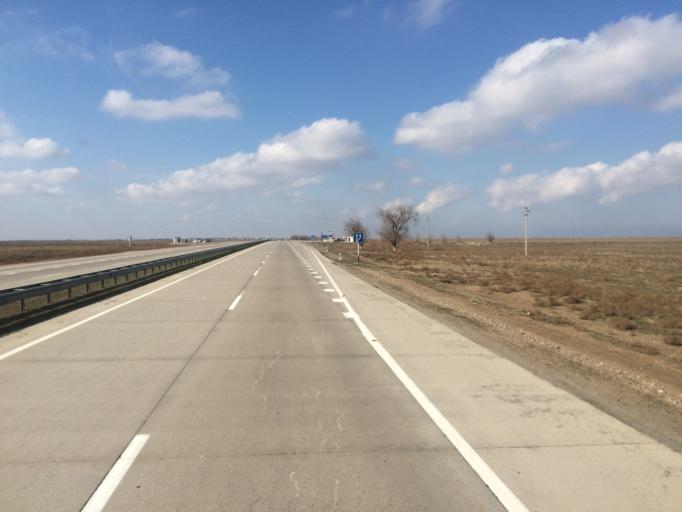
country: KZ
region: Ongtustik Qazaqstan
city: Temirlanovka
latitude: 42.8438
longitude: 69.0988
